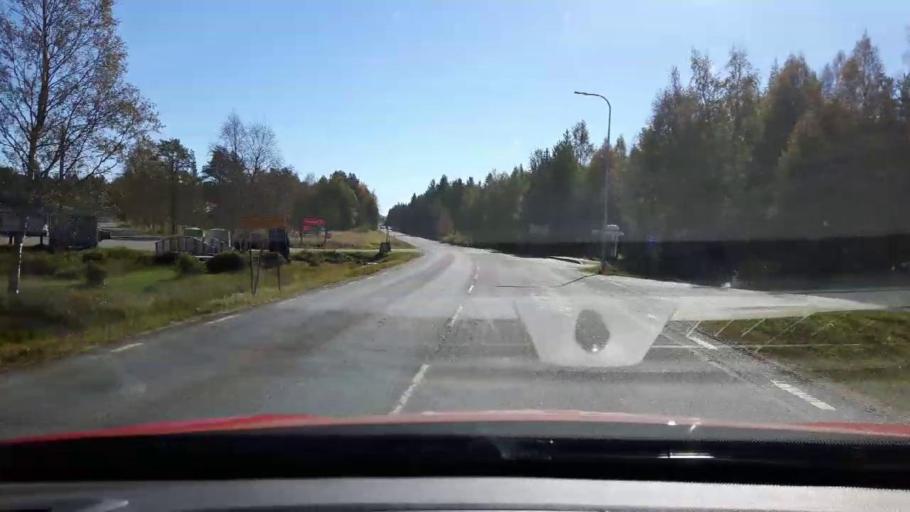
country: SE
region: Jaemtland
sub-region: Harjedalens Kommun
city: Sveg
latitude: 62.3099
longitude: 14.0413
